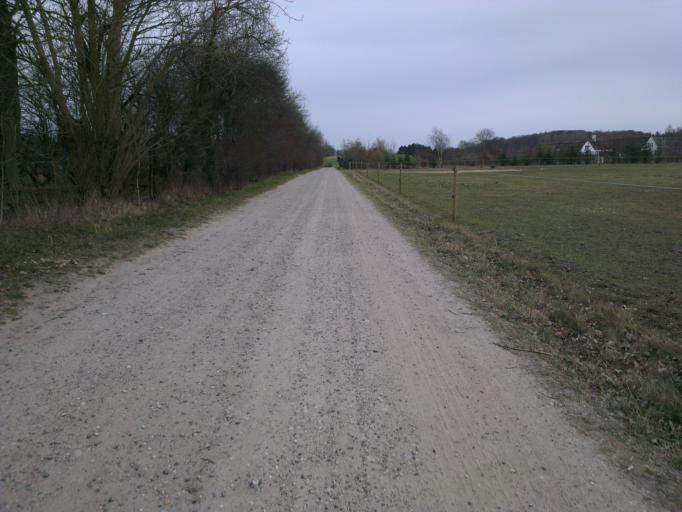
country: DK
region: Capital Region
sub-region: Frederikssund Kommune
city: Frederikssund
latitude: 55.8379
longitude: 12.0187
